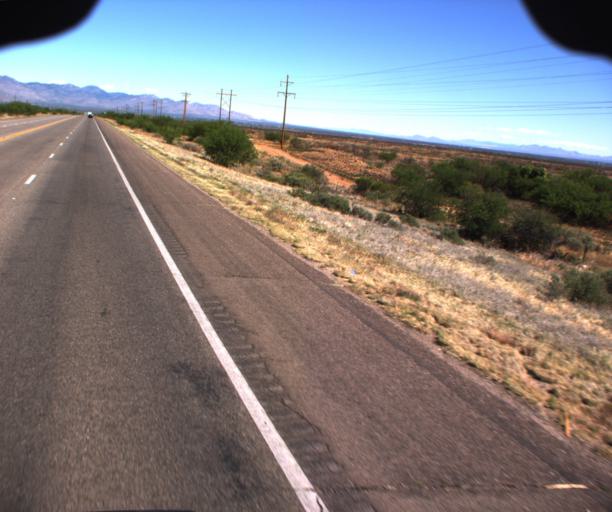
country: US
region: Arizona
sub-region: Cochise County
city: Huachuca City
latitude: 31.5955
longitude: -110.3251
